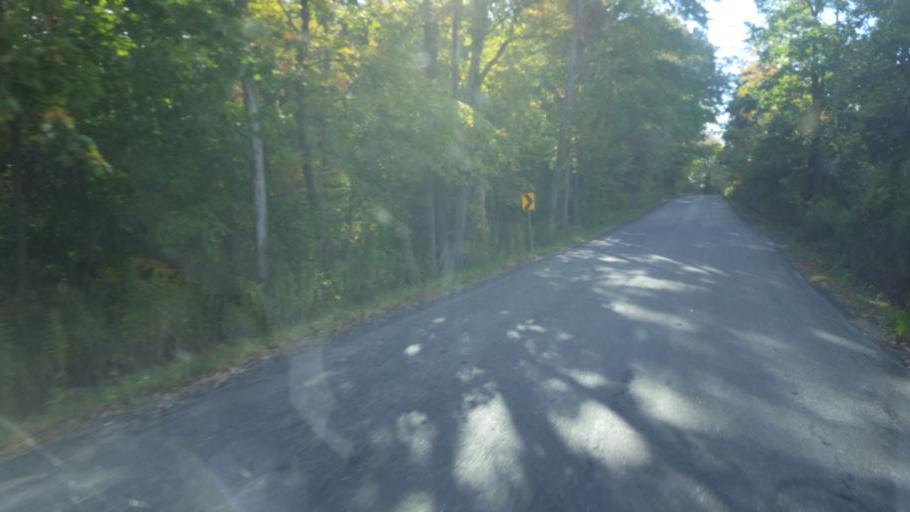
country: US
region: Pennsylvania
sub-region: Mercer County
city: Mercer
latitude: 41.3647
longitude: -80.2492
